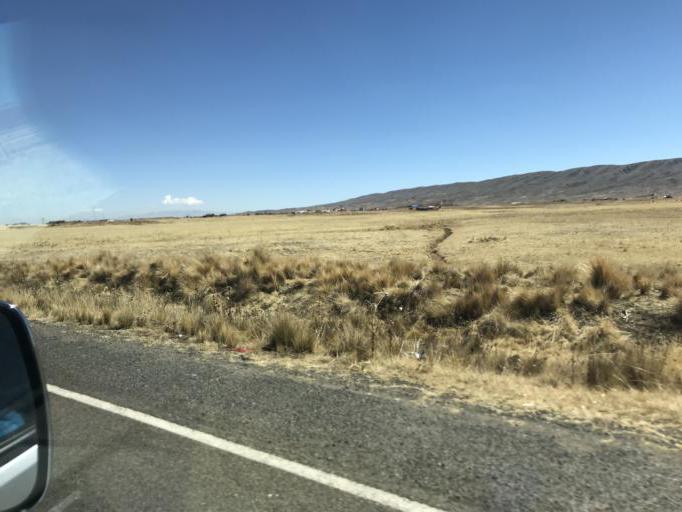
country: BO
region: La Paz
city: Tiahuanaco
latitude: -16.5691
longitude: -68.6615
